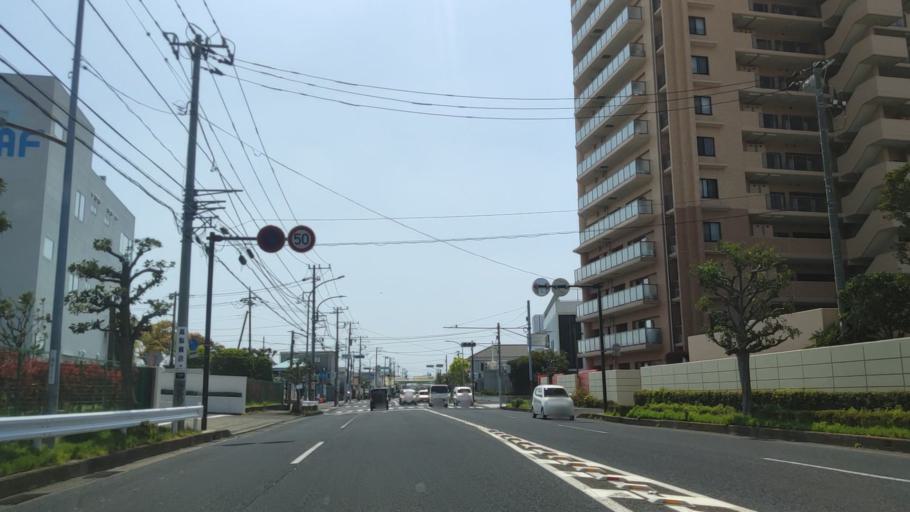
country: JP
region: Kanagawa
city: Hiratsuka
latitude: 35.3268
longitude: 139.3602
